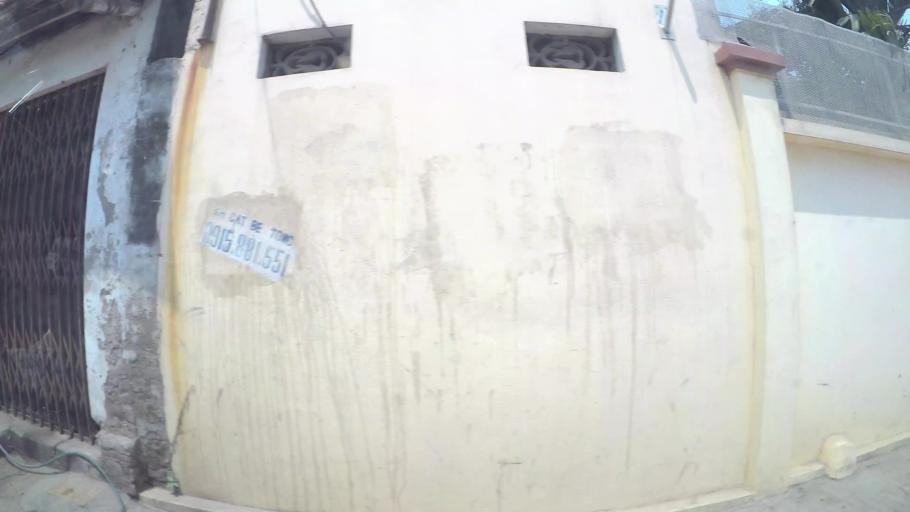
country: VN
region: Ha Noi
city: Van Dien
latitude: 20.9520
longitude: 105.8288
